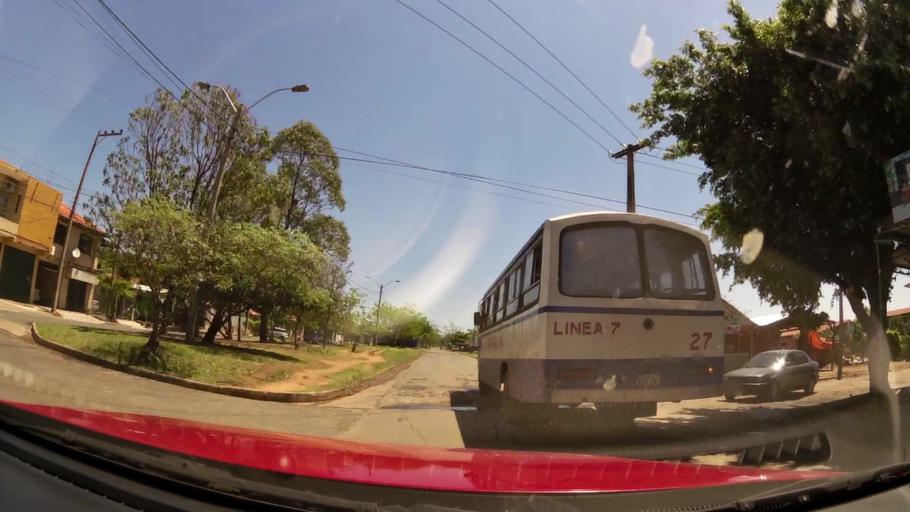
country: PY
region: Central
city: Colonia Mariano Roque Alonso
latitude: -25.2332
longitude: -57.5483
